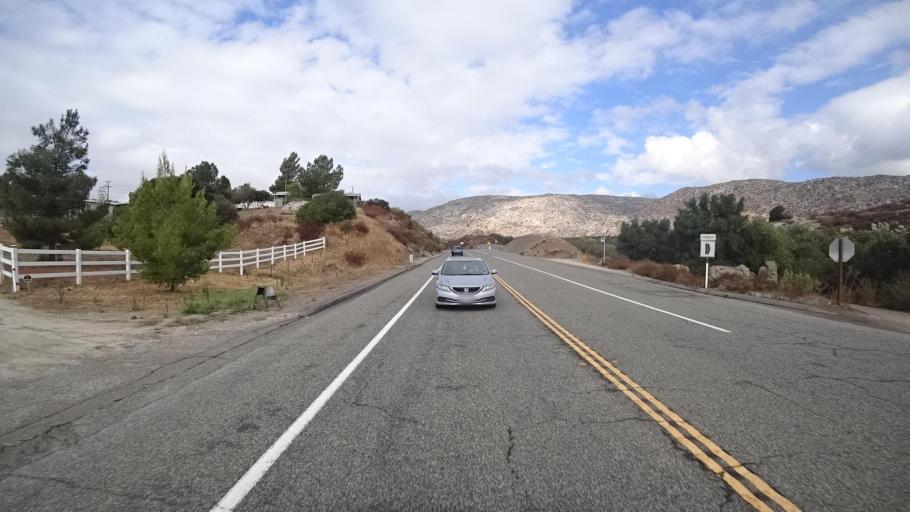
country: MX
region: Baja California
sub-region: Tecate
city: Hacienda Tecate
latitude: 32.5898
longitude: -116.5214
